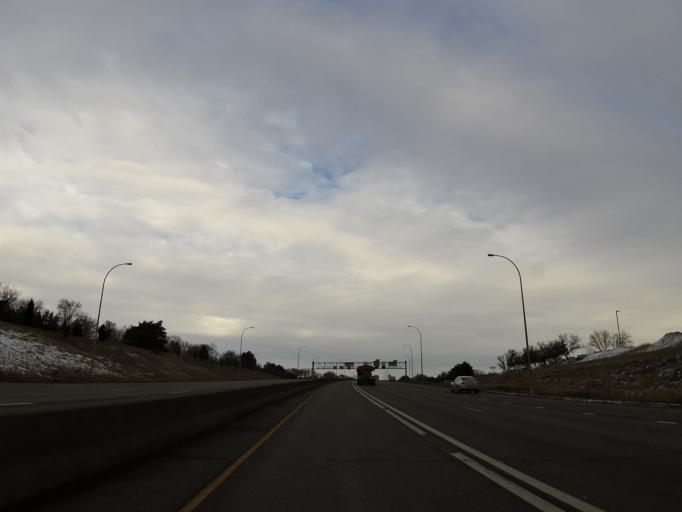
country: US
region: Minnesota
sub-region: Hennepin County
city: Bloomington
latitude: 44.8074
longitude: -93.2913
